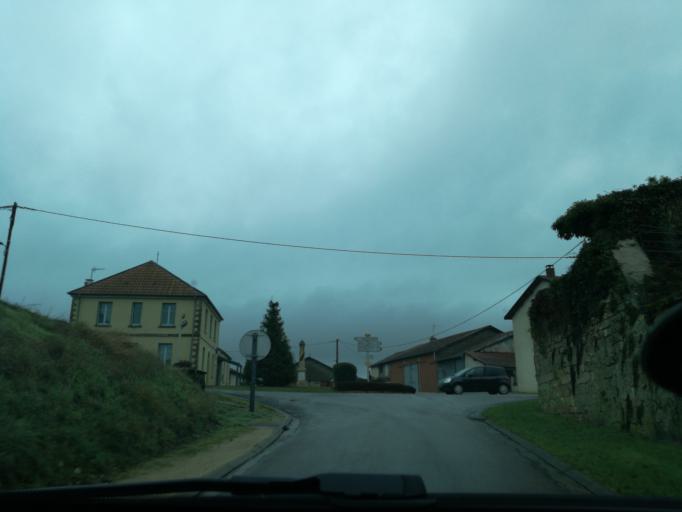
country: FR
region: Lorraine
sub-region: Departement de la Meuse
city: Revigny-sur-Ornain
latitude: 48.8668
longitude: 5.0764
